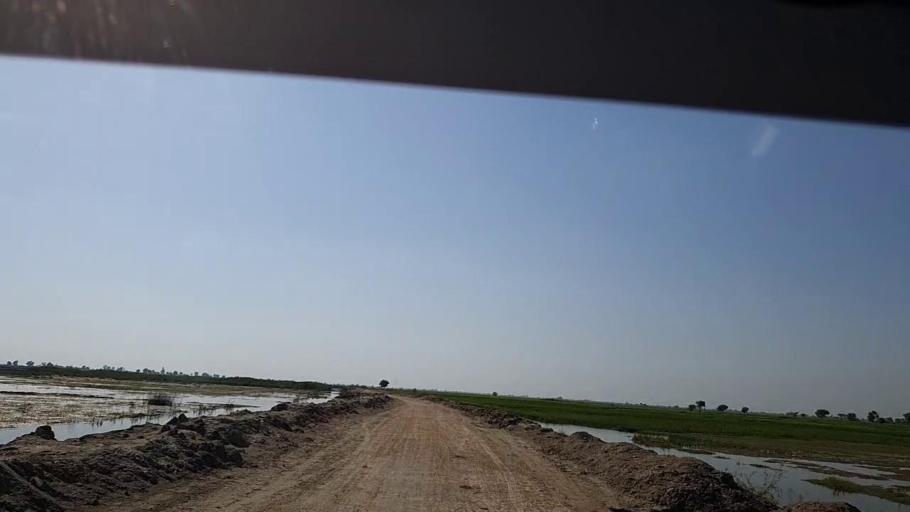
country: PK
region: Sindh
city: Tangwani
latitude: 28.3521
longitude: 69.0490
